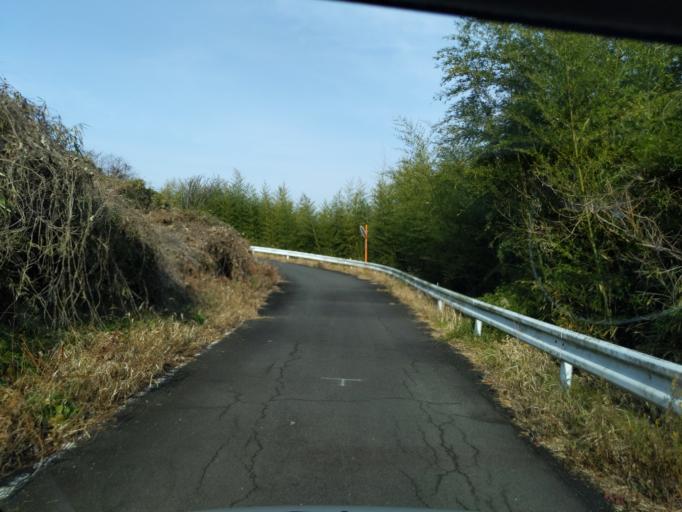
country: JP
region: Miyagi
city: Wakuya
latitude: 38.6991
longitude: 141.1481
